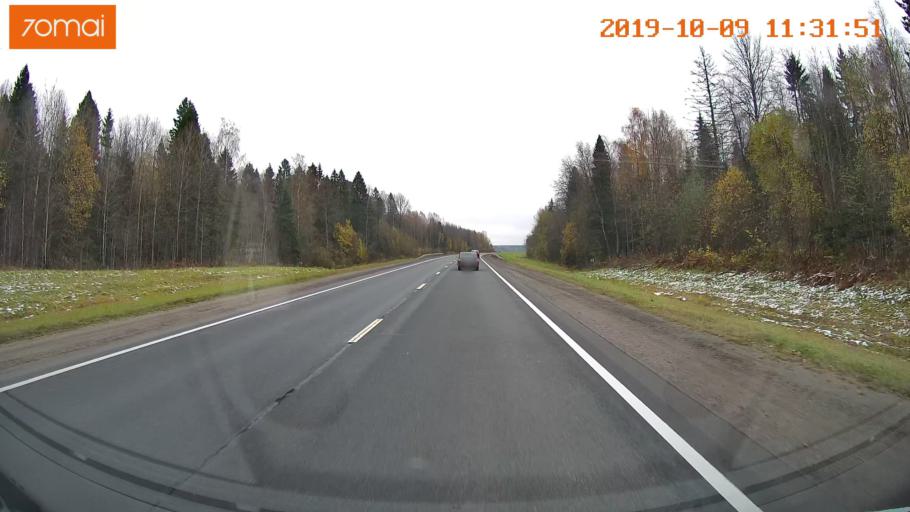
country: RU
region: Vologda
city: Gryazovets
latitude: 59.0416
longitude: 40.1029
